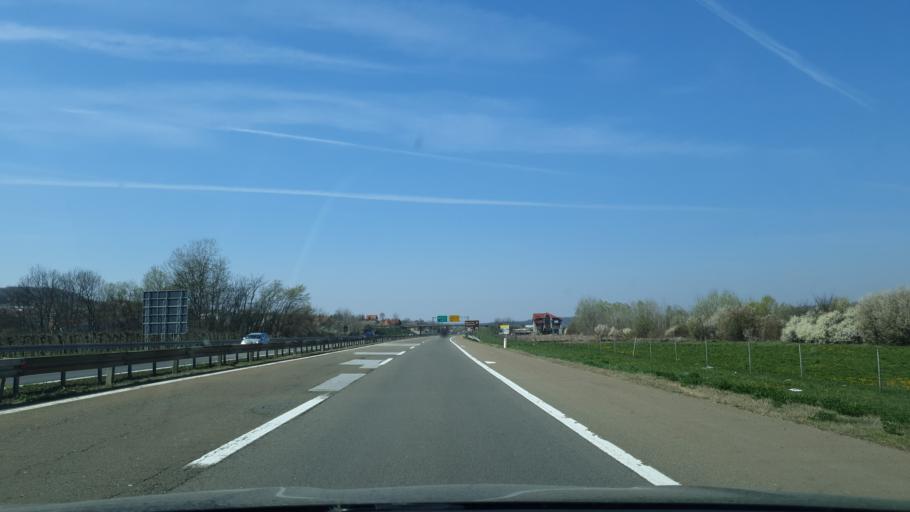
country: RS
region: Central Serbia
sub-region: Belgrade
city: Grocka
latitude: 44.5752
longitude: 20.7522
